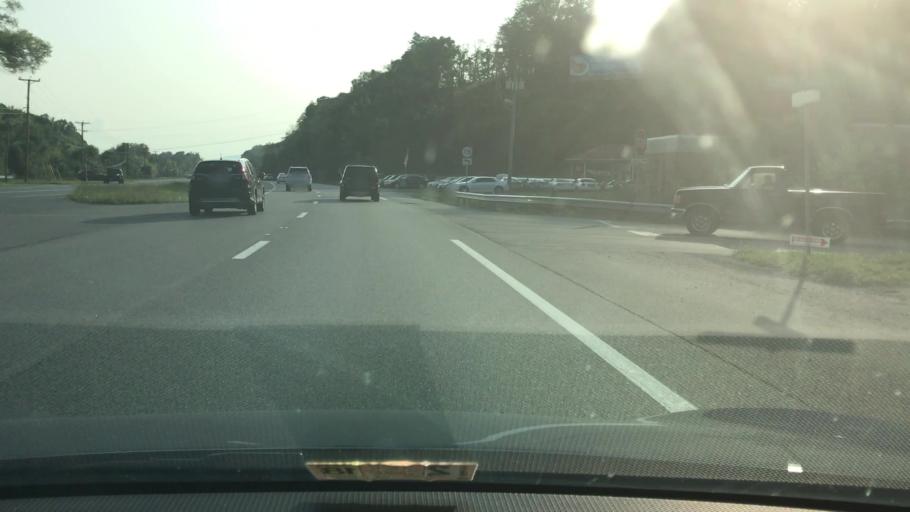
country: US
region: Virginia
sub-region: Botetourt County
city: Laymantown
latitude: 37.3359
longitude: -79.8586
